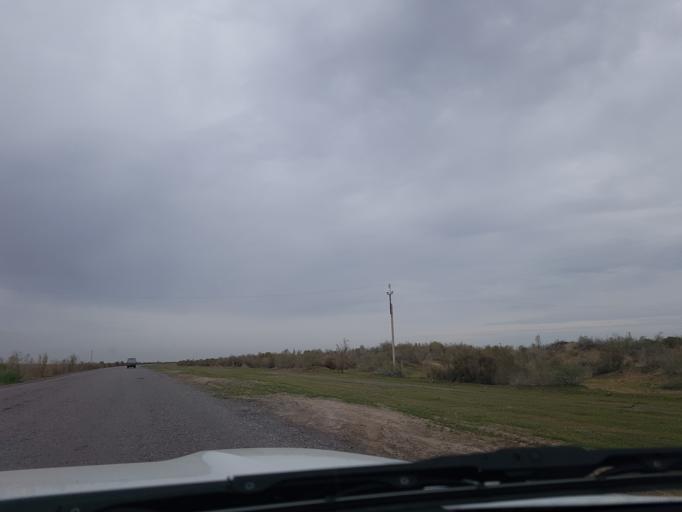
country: TM
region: Lebap
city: Turkmenabat
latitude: 38.8511
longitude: 63.4048
